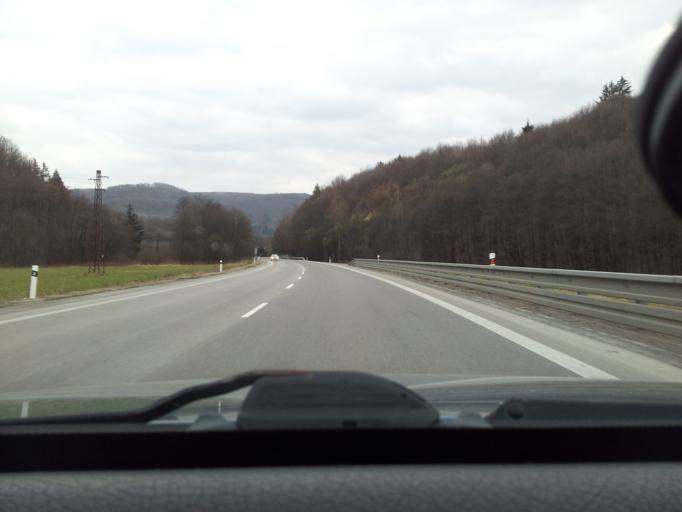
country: SK
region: Banskobystricky
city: Ziar nad Hronom
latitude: 48.6381
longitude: 18.9010
